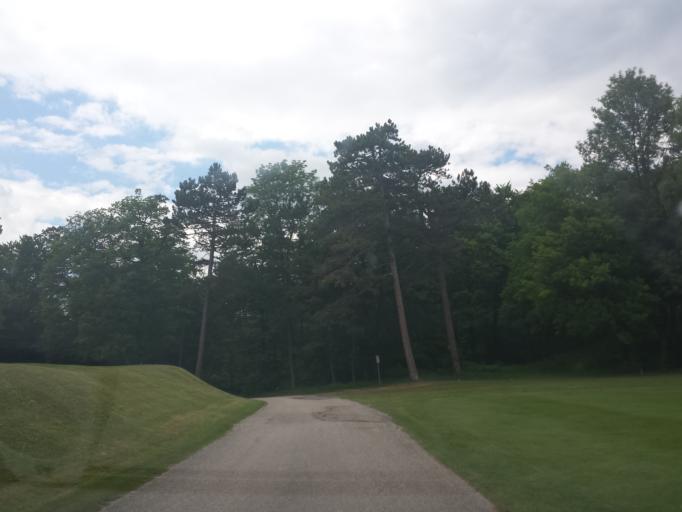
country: AT
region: Lower Austria
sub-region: Politischer Bezirk Baden
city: Hirtenberg
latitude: 47.9208
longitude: 16.1503
